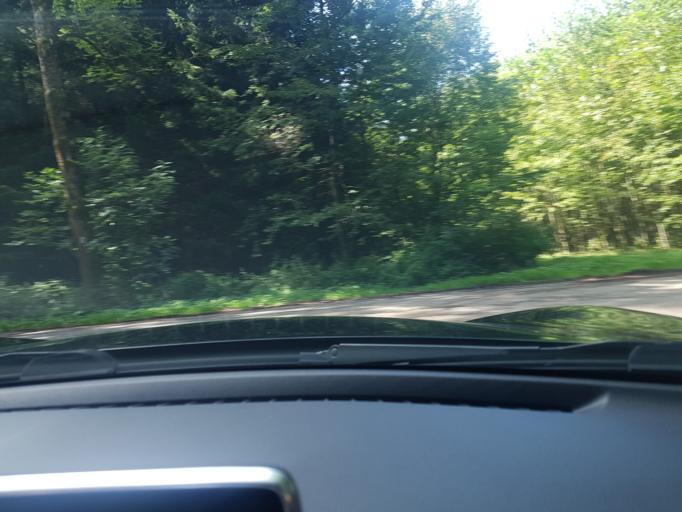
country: DE
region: Baden-Wuerttemberg
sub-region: Karlsruhe Region
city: Limbach
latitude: 49.4945
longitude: 9.2565
